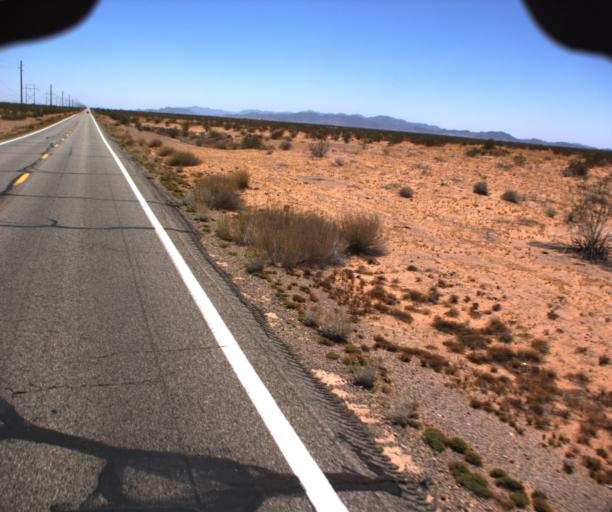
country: US
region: Arizona
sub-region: La Paz County
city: Quartzsite
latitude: 33.8777
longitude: -114.2170
